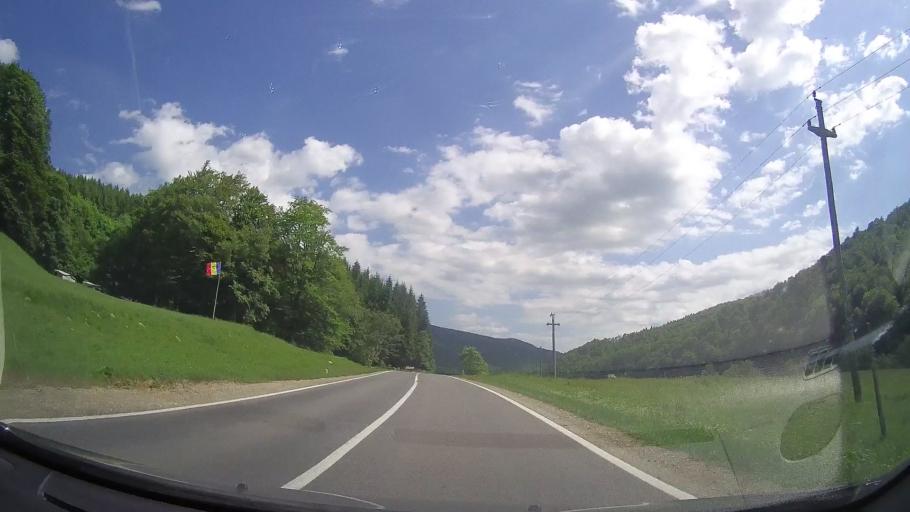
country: RO
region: Prahova
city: Maneciu
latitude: 45.4323
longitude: 25.9385
